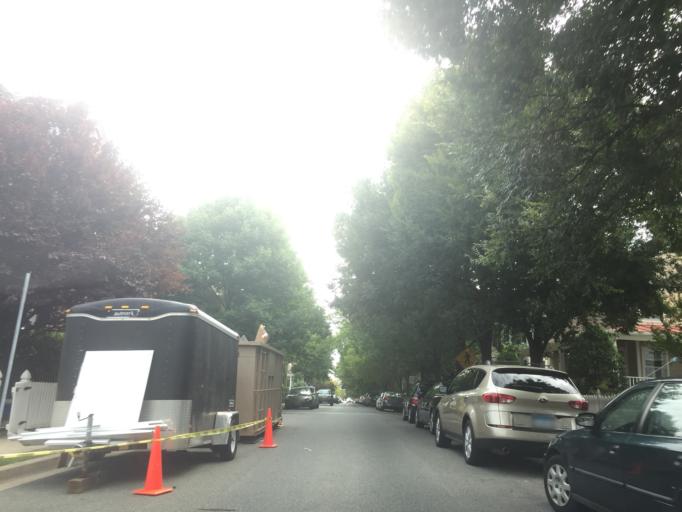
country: US
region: Maryland
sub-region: Montgomery County
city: North Potomac
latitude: 39.1209
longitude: -77.2452
